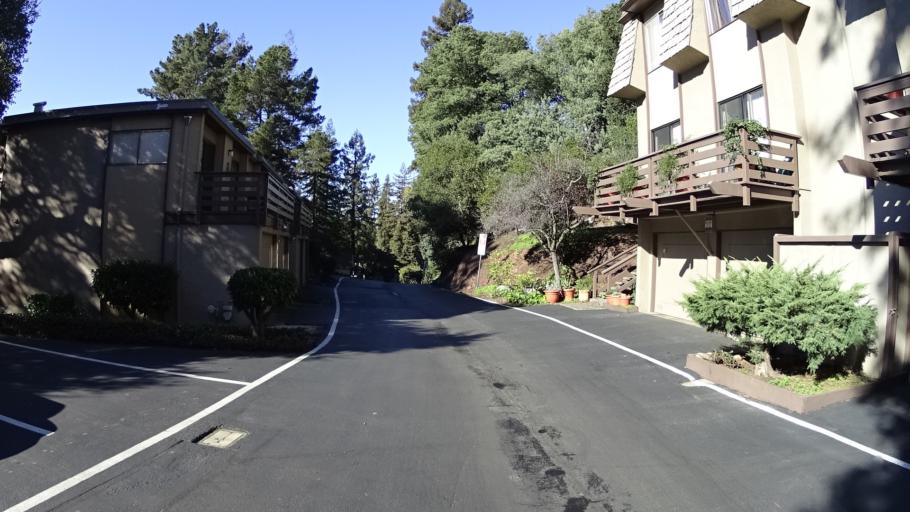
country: US
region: California
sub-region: Alameda County
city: Piedmont
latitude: 37.8380
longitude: -122.2329
